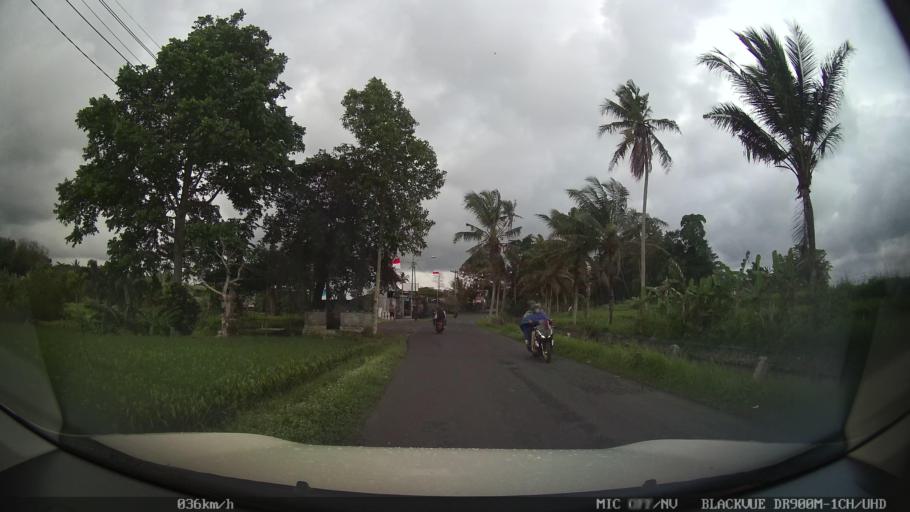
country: ID
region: Bali
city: Banjar Cemenggon
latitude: -8.5514
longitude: 115.1937
